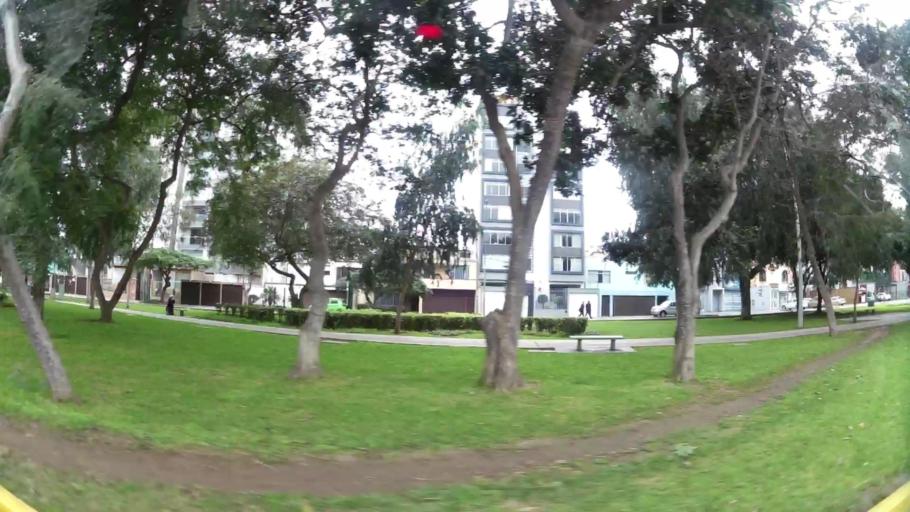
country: PE
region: Lima
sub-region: Lima
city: San Luis
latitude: -12.1013
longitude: -77.0029
